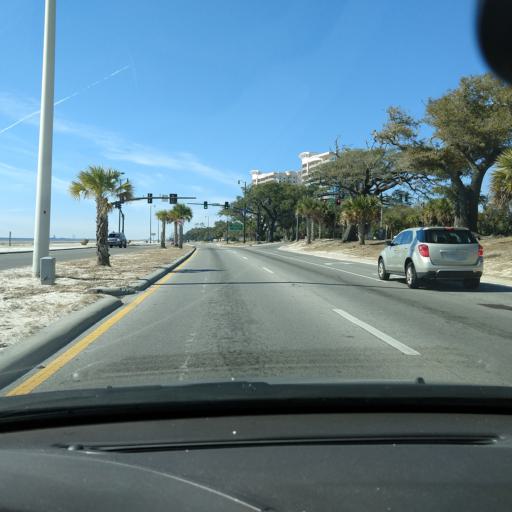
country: US
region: Mississippi
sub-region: Harrison County
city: Gulfport
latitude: 30.3882
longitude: -89.0004
